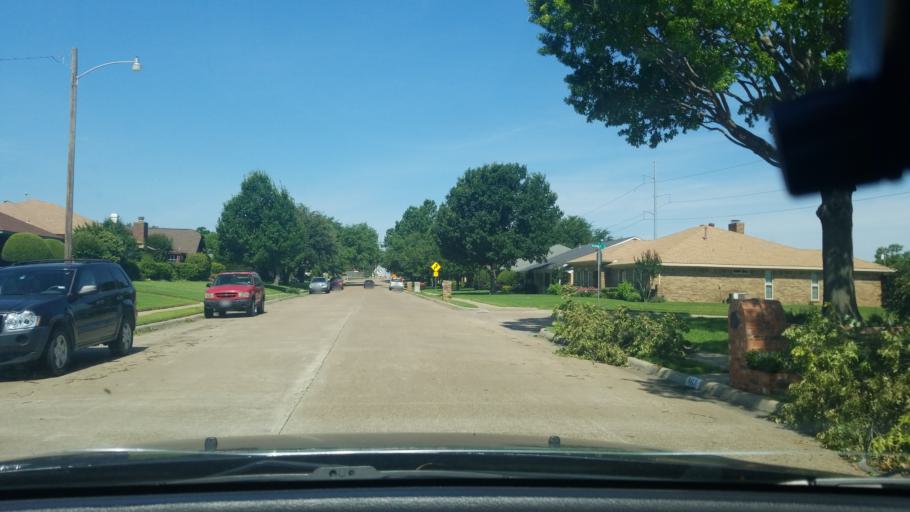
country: US
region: Texas
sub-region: Dallas County
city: Mesquite
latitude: 32.7751
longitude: -96.5920
